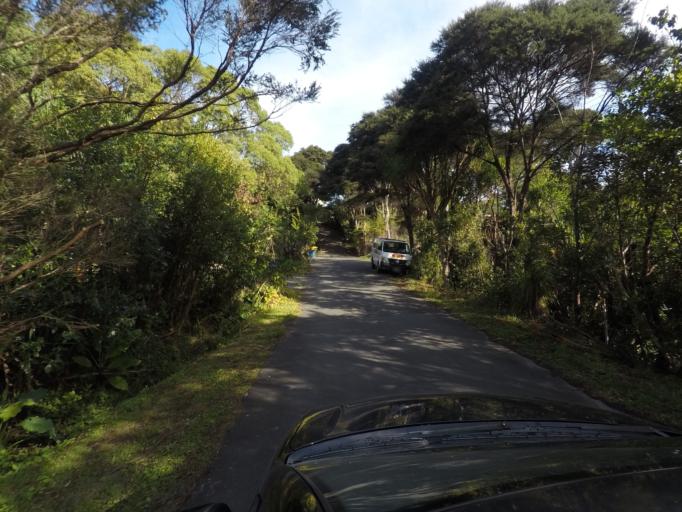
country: NZ
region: Auckland
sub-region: Auckland
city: Titirangi
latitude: -36.9984
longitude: 174.5746
